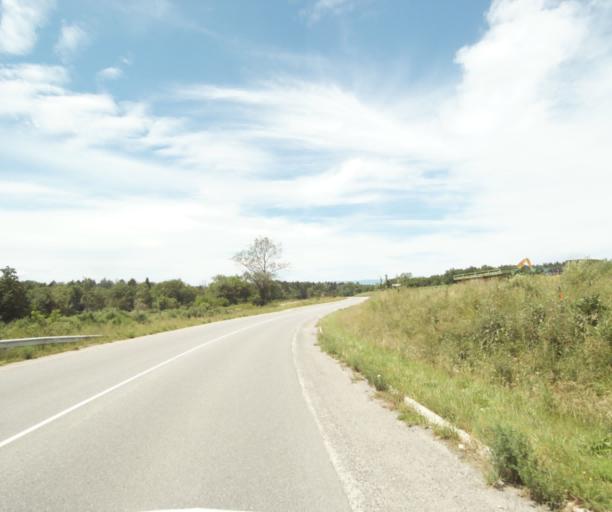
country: FR
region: Rhone-Alpes
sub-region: Departement de la Haute-Savoie
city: Margencel
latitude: 46.3227
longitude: 6.4371
